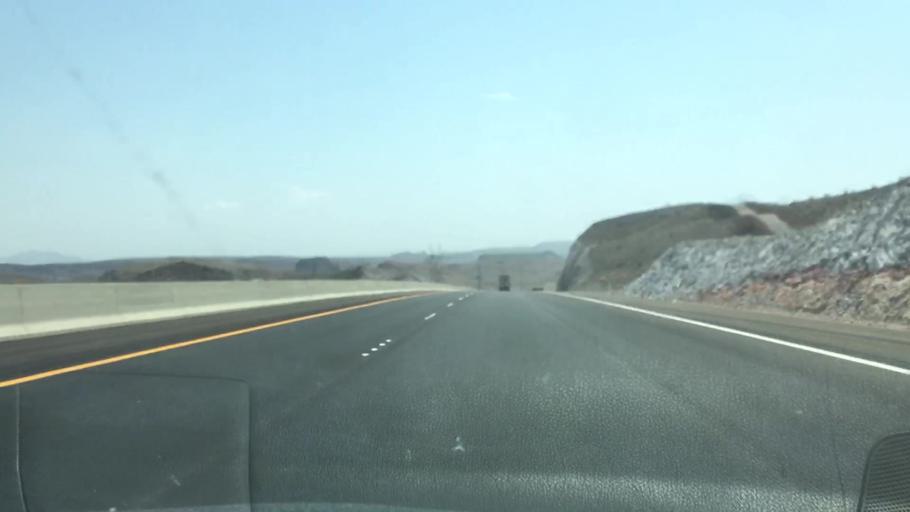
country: US
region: Nevada
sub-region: Clark County
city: Boulder City
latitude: 35.9886
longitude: -114.7977
